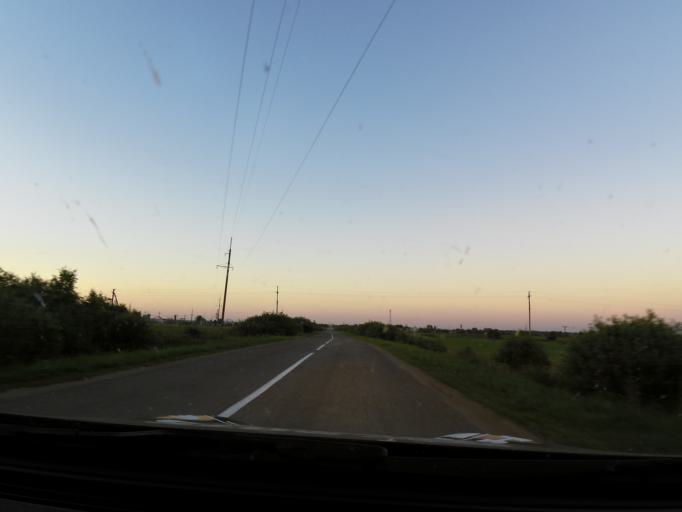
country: RU
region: Jaroslavl
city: Lyubim
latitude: 58.3177
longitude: 40.9936
